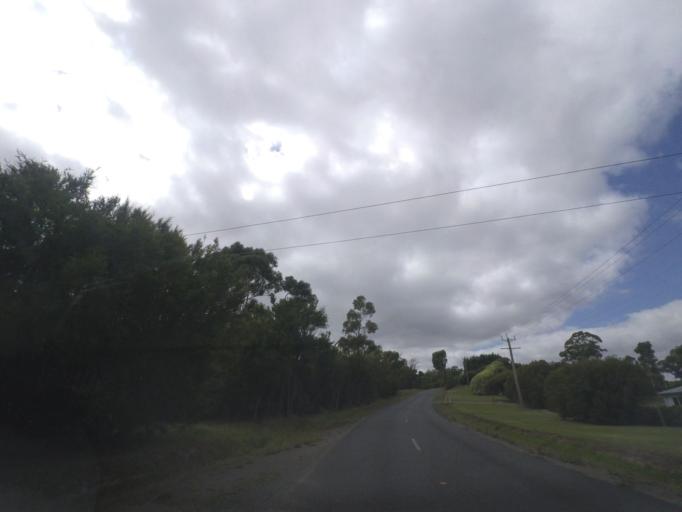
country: AU
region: Victoria
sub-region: Yarra Ranges
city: Woori Yallock
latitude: -37.7730
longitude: 145.5430
